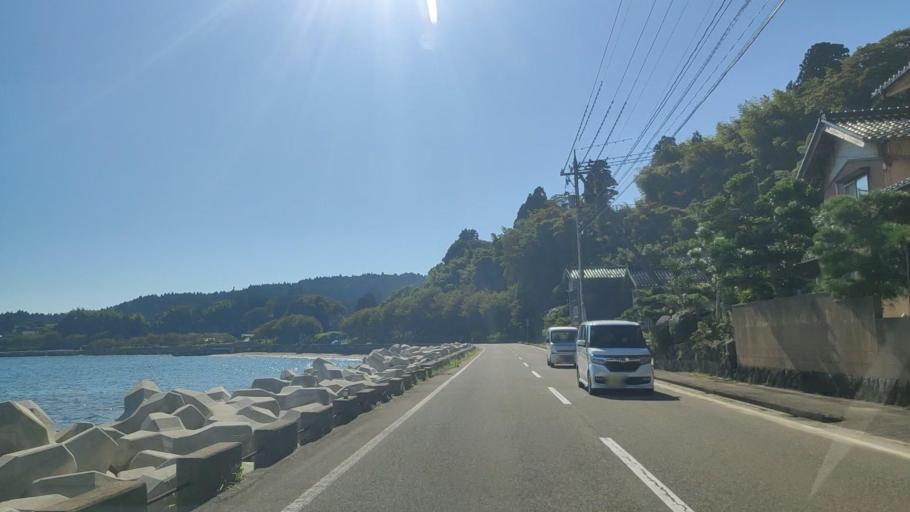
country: JP
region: Ishikawa
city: Nanao
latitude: 37.2794
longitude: 137.0998
